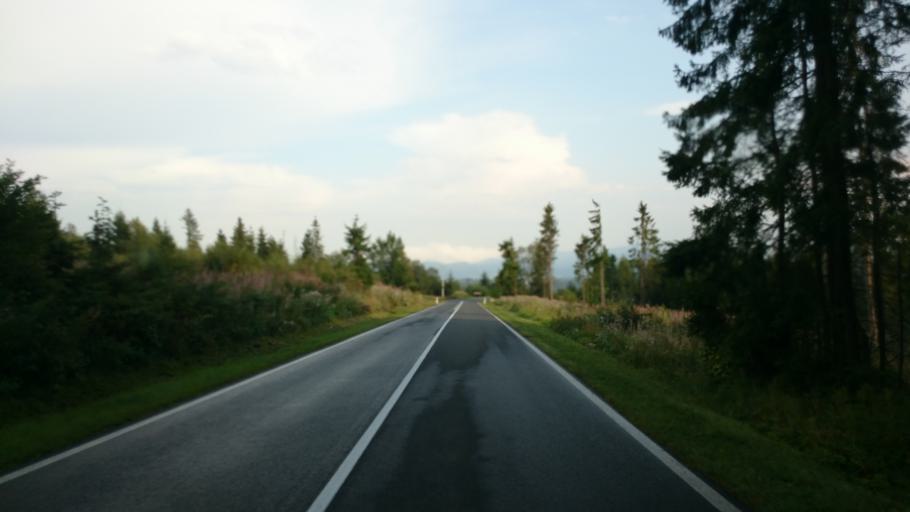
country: SK
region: Presovsky
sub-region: Okres Poprad
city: Strba
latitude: 49.0984
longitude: 20.0675
